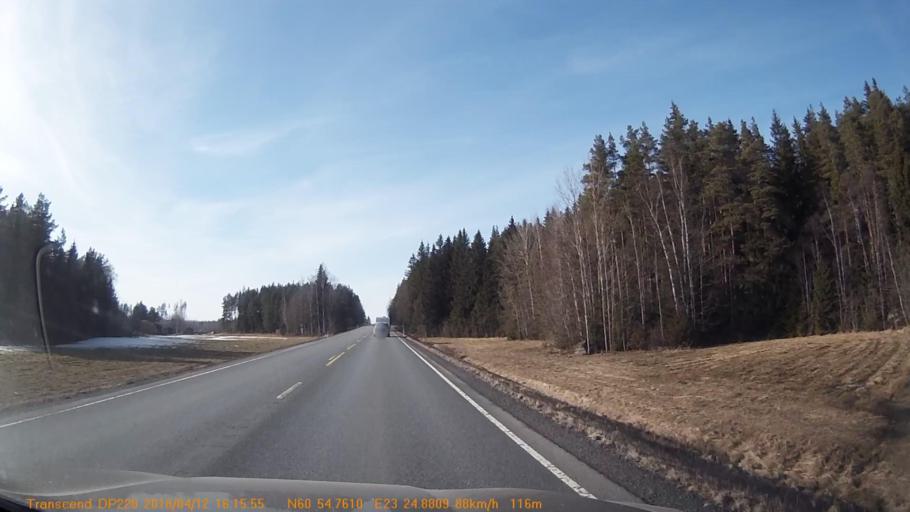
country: FI
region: Haeme
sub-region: Forssa
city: Humppila
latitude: 60.9129
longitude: 23.4144
